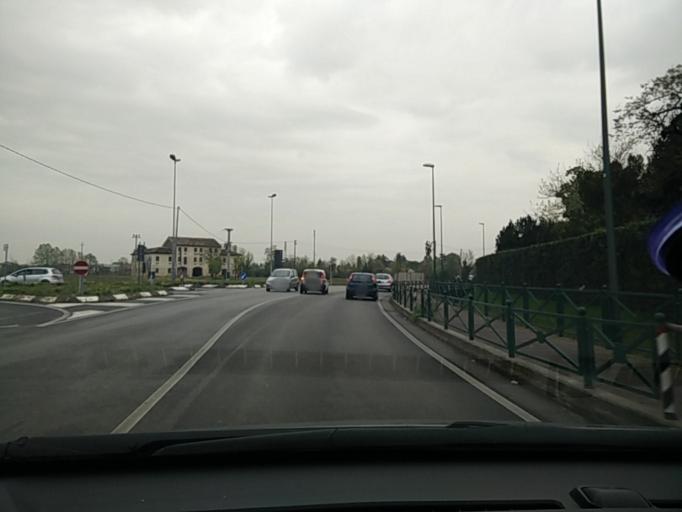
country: IT
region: Veneto
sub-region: Provincia di Treviso
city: Lancenigo-Villorba
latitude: 45.7156
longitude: 12.2758
